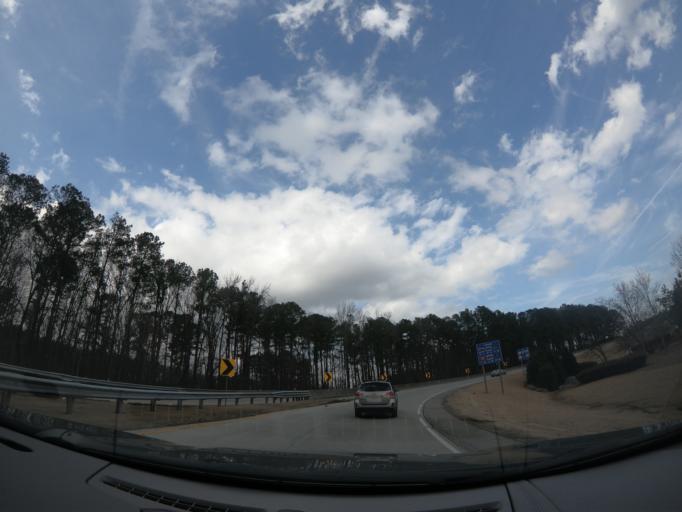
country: US
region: Georgia
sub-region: Fulton County
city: Alpharetta
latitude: 34.0549
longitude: -84.2882
